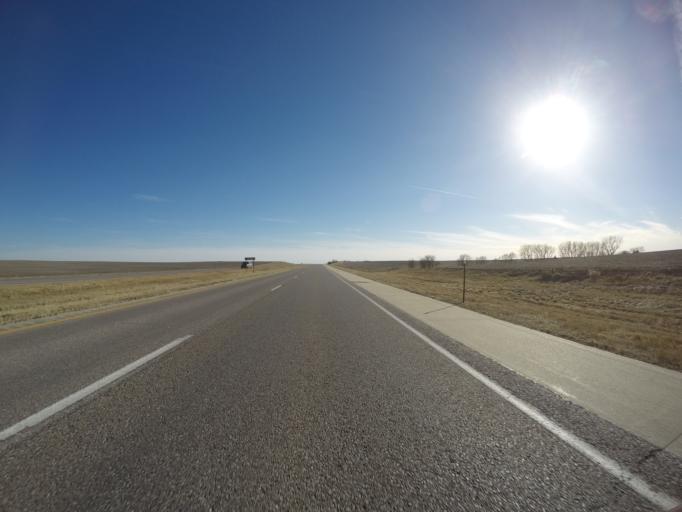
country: US
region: Nebraska
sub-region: Gage County
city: Beatrice
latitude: 40.4201
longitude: -96.7425
